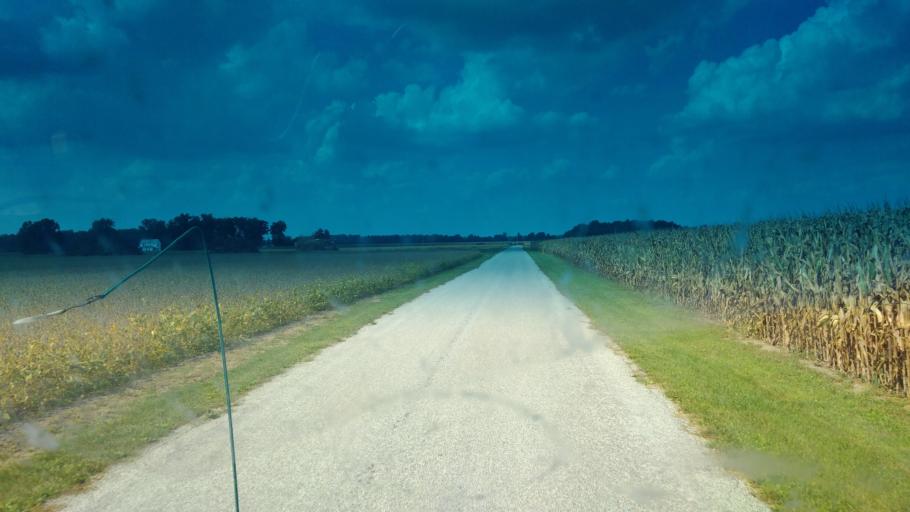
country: US
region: Ohio
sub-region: Hardin County
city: Kenton
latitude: 40.7275
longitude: -83.6145
